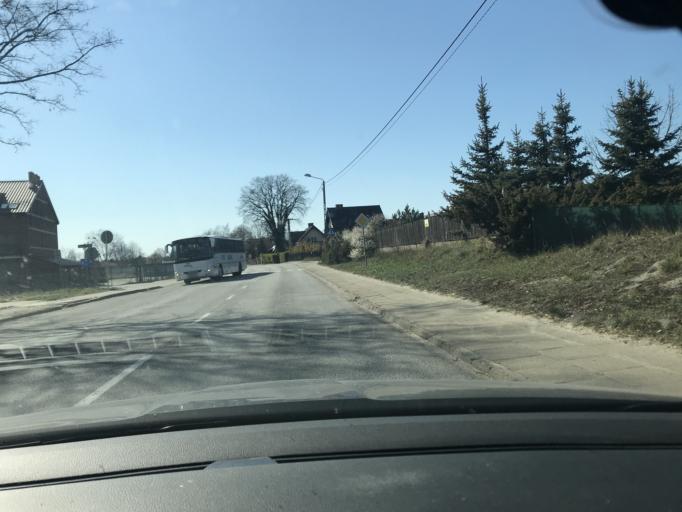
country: PL
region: Pomeranian Voivodeship
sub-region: Powiat nowodworski
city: Sztutowo
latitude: 54.3328
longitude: 19.1836
